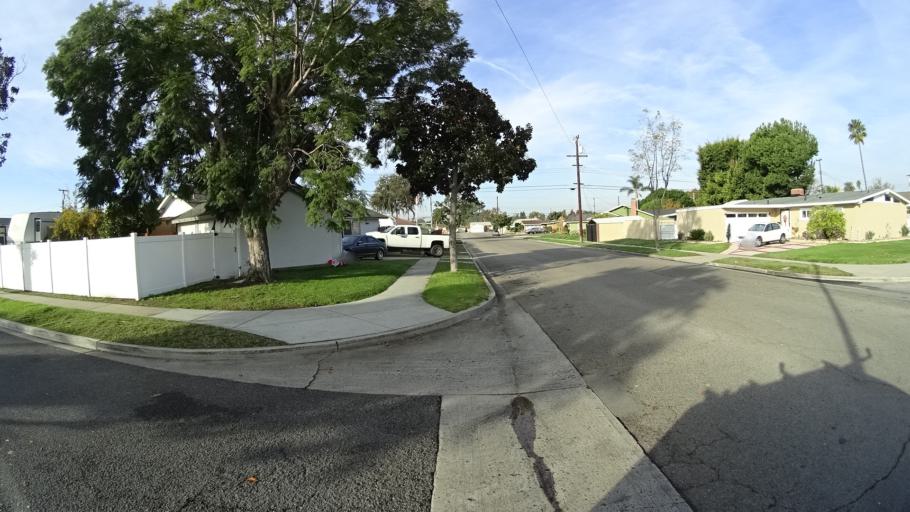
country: US
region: California
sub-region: Orange County
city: Garden Grove
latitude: 33.7915
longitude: -117.9218
